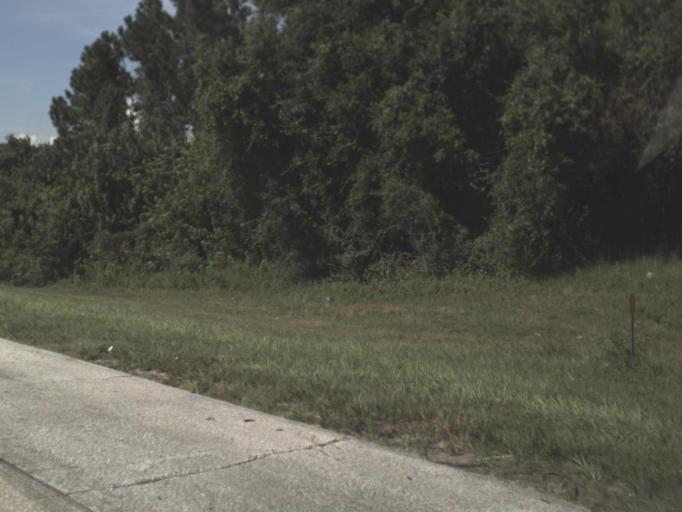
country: US
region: Florida
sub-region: Hillsborough County
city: Mango
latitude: 27.9810
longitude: -82.3266
